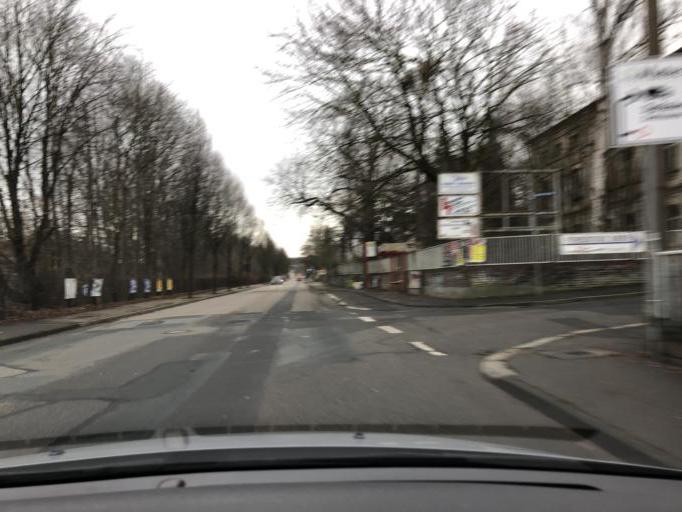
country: DE
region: Saxony
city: Dobeln
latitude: 51.1162
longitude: 13.1241
